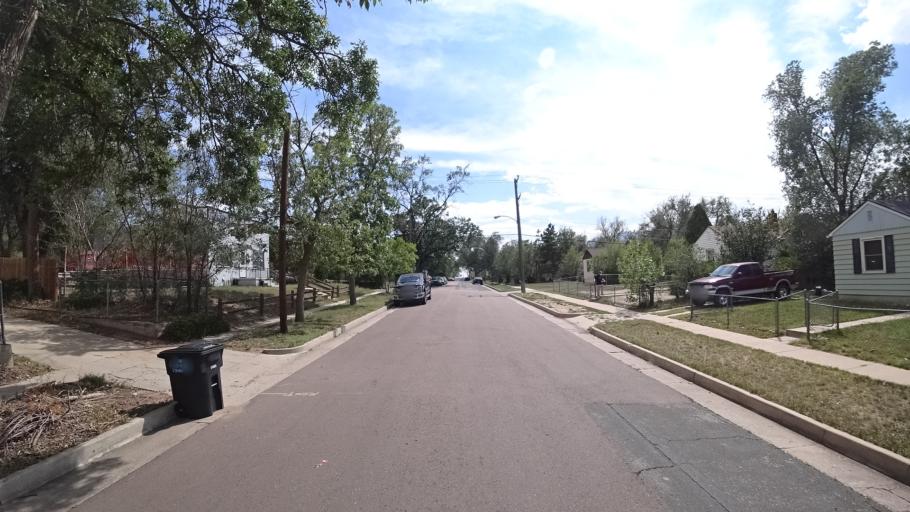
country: US
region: Colorado
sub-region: El Paso County
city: Colorado Springs
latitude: 38.8237
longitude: -104.8108
